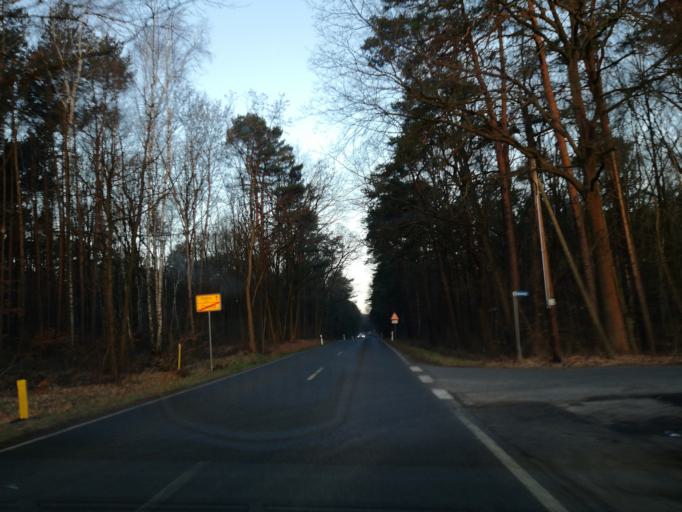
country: DE
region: Brandenburg
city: Crinitz
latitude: 51.7374
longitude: 13.7522
